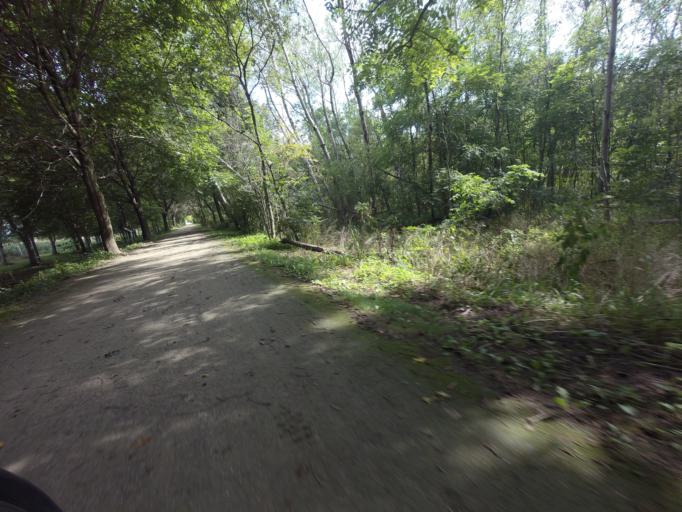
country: CA
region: Ontario
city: Waterloo
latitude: 43.6066
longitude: -80.5611
